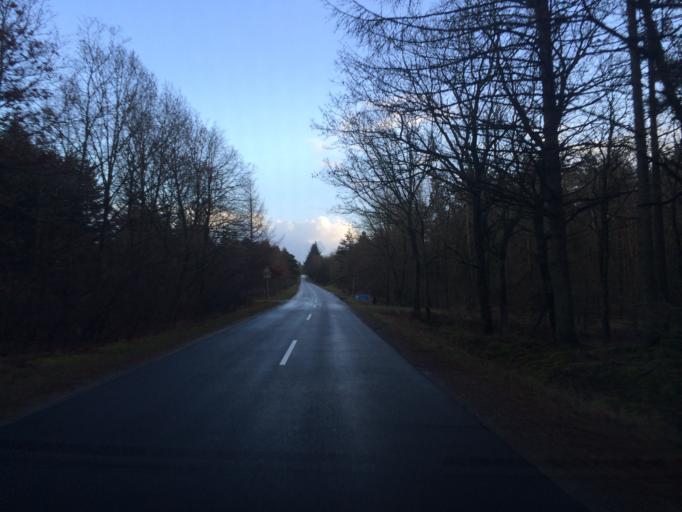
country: DK
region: Central Jutland
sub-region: Holstebro Kommune
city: Ulfborg
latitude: 56.2506
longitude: 8.3697
